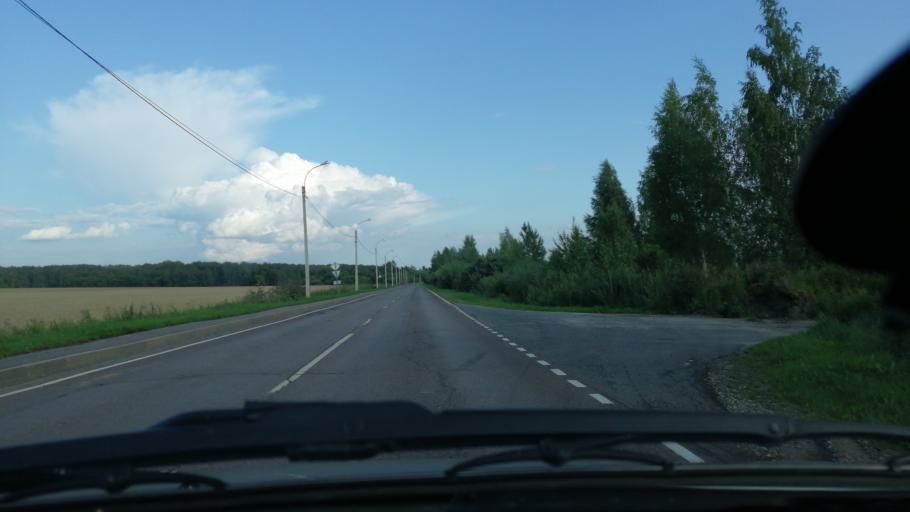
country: RU
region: Moskovskaya
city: Troitskoye
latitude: 55.2878
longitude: 38.5357
